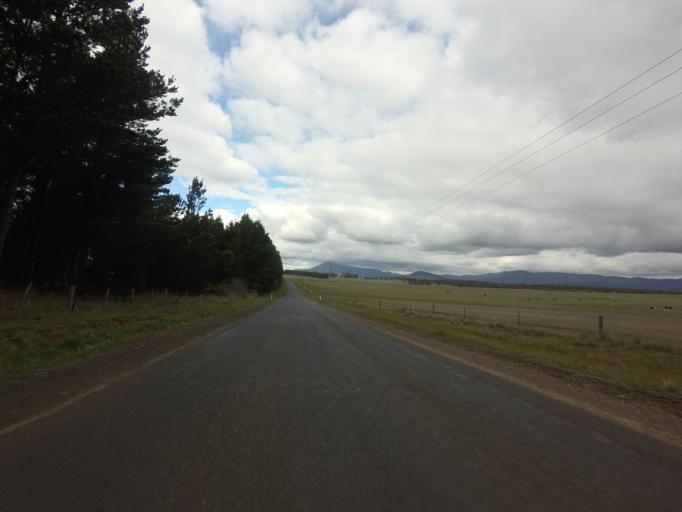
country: AU
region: Tasmania
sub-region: Northern Midlands
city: Longford
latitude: -41.7690
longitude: 147.0870
